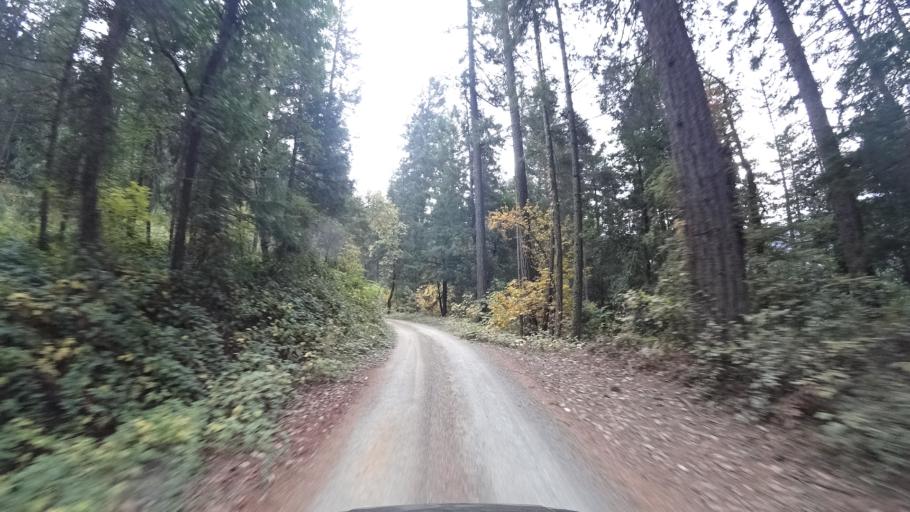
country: US
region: California
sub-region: Siskiyou County
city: Happy Camp
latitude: 41.7915
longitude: -123.3391
